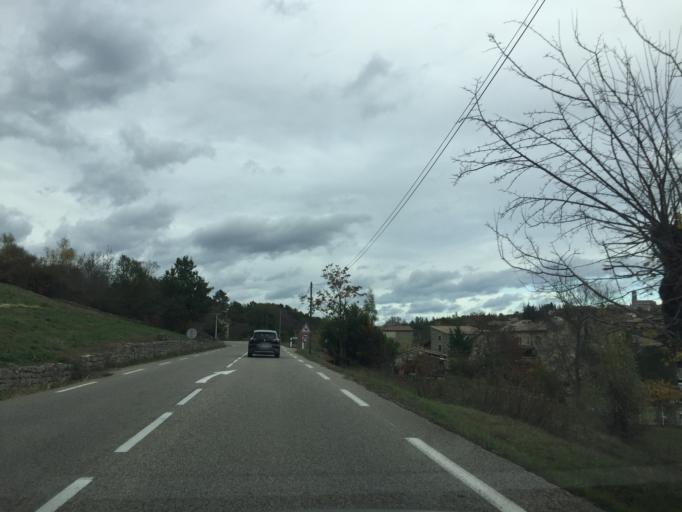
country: FR
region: Rhone-Alpes
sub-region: Departement de l'Ardeche
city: Lablachere
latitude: 44.4484
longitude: 4.2102
